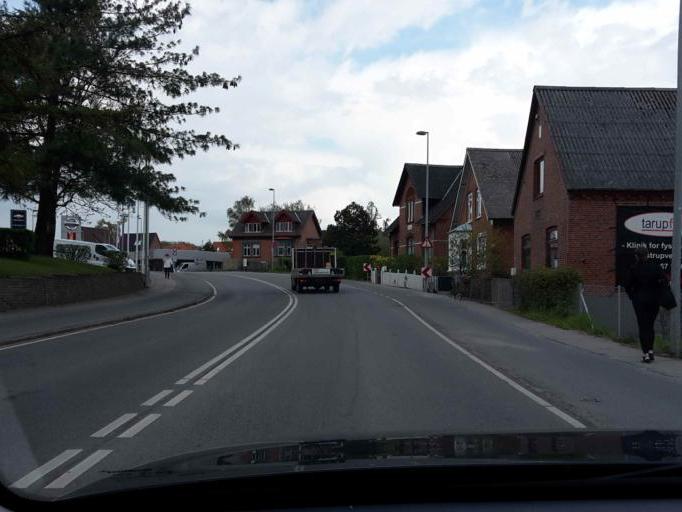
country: DK
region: South Denmark
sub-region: Odense Kommune
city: Odense
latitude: 55.4030
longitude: 10.3561
